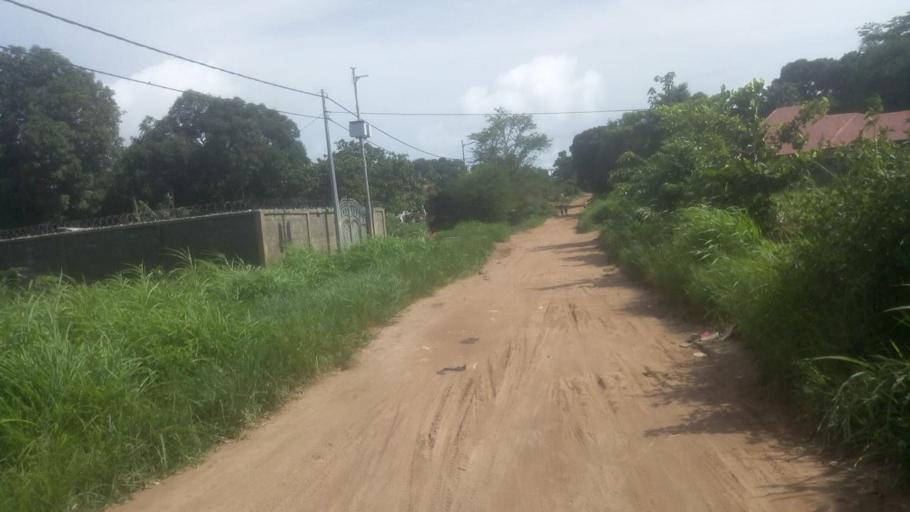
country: SL
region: Northern Province
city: Masoyila
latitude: 8.6103
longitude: -13.1950
